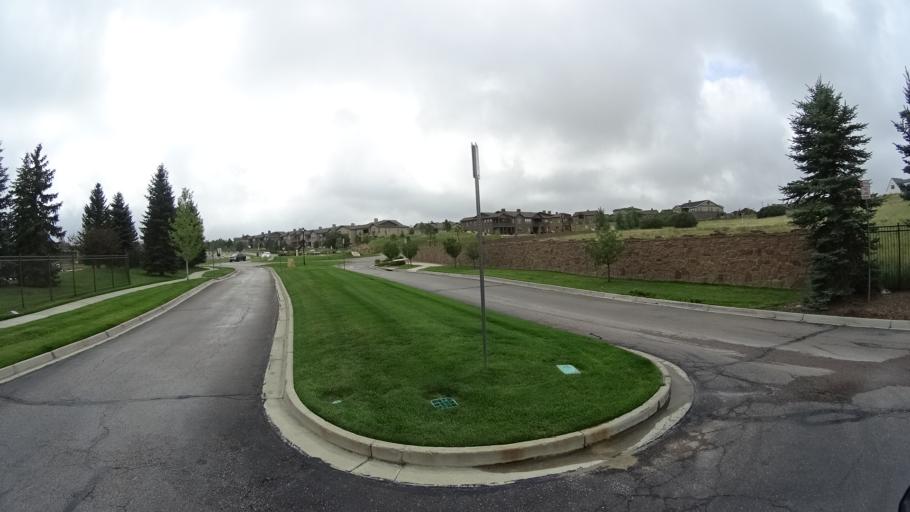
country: US
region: Colorado
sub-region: El Paso County
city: Gleneagle
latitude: 39.0171
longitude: -104.7909
